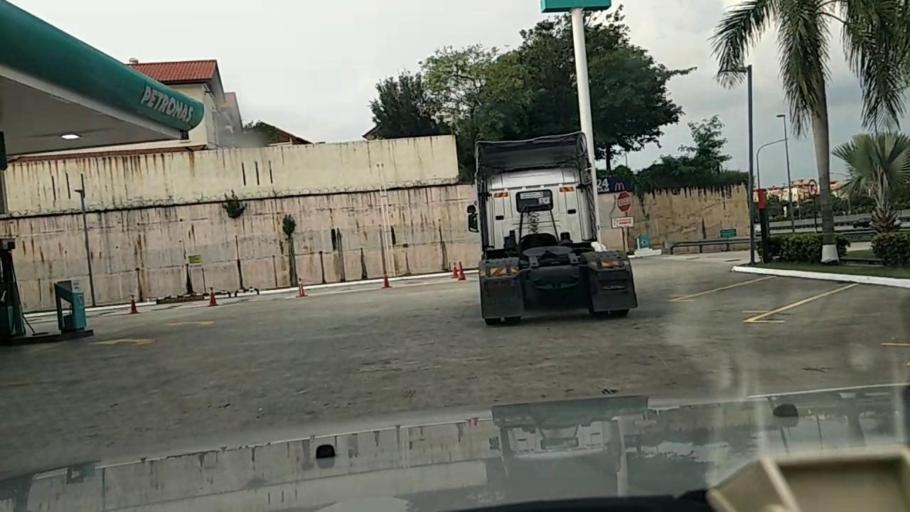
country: MY
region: Selangor
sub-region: Petaling
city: Petaling Jaya
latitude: 3.1192
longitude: 101.5931
